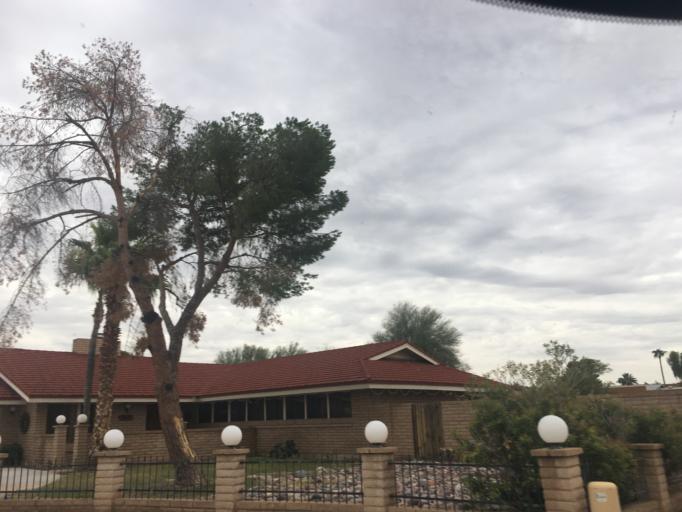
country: US
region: Arizona
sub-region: Maricopa County
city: Guadalupe
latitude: 33.3650
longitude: -111.9265
